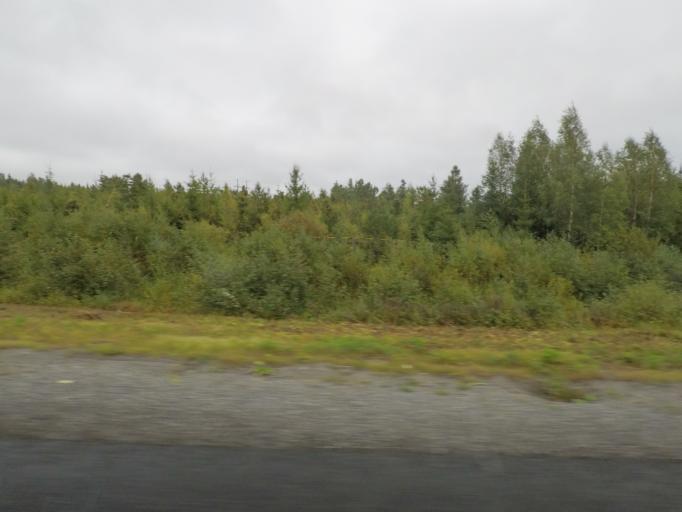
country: FI
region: Northern Savo
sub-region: Kuopio
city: Kuopio
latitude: 62.7552
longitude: 27.5805
